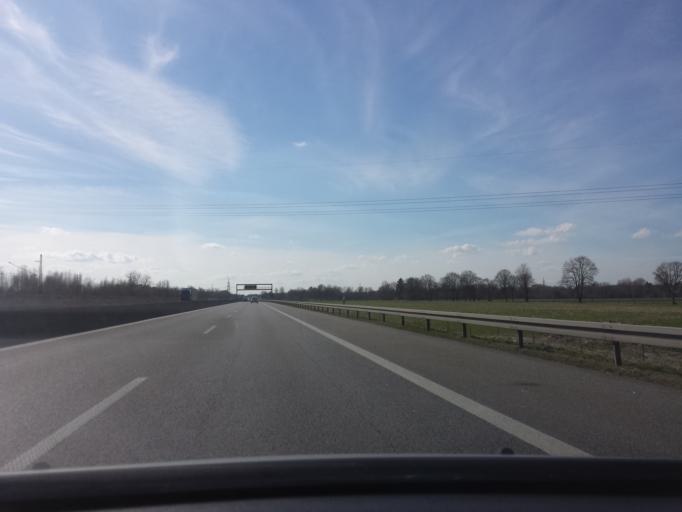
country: DE
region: Bavaria
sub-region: Upper Bavaria
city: Karlsfeld
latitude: 48.2048
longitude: 11.4257
